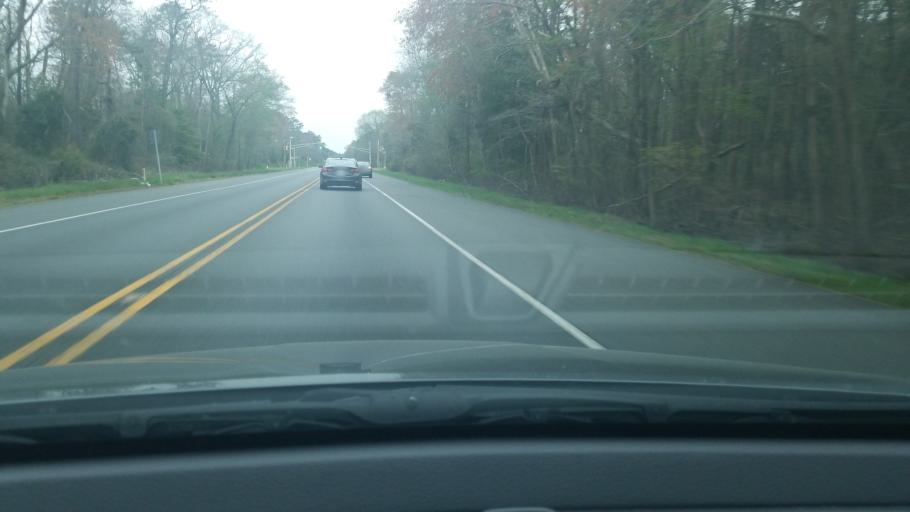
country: US
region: New Jersey
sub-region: Burlington County
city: Leisuretowne
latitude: 39.8860
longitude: -74.7197
